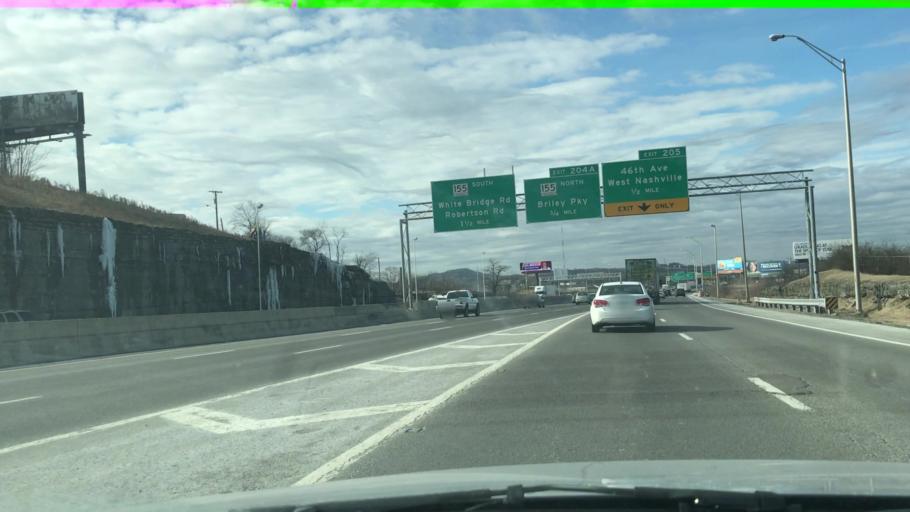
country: US
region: Tennessee
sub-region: Davidson County
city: Nashville
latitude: 36.1557
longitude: -86.8287
